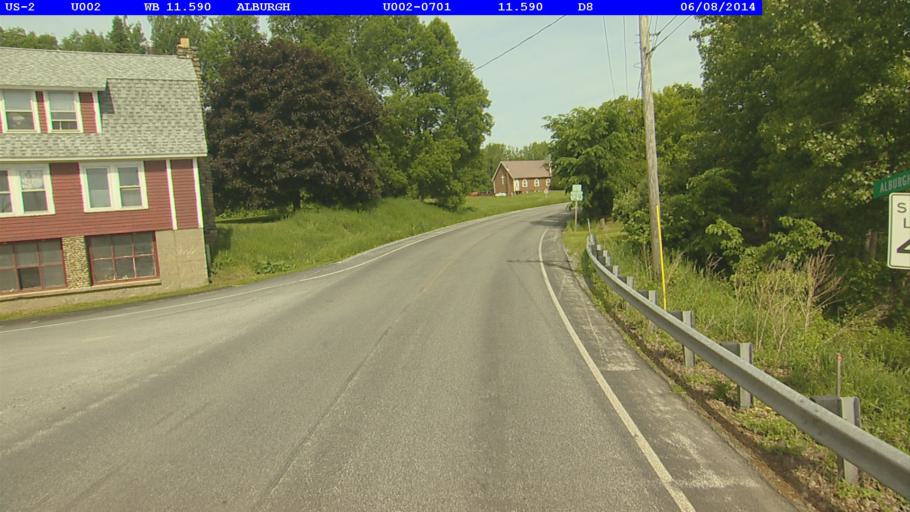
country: US
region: Vermont
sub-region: Grand Isle County
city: North Hero
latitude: 44.8864
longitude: -73.2774
